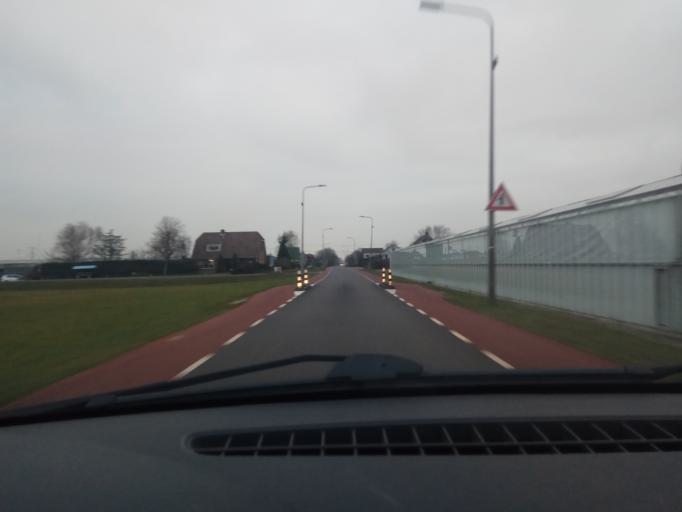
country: NL
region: South Holland
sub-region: Gemeente Westland
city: Maasdijk
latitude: 51.9617
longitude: 4.2055
